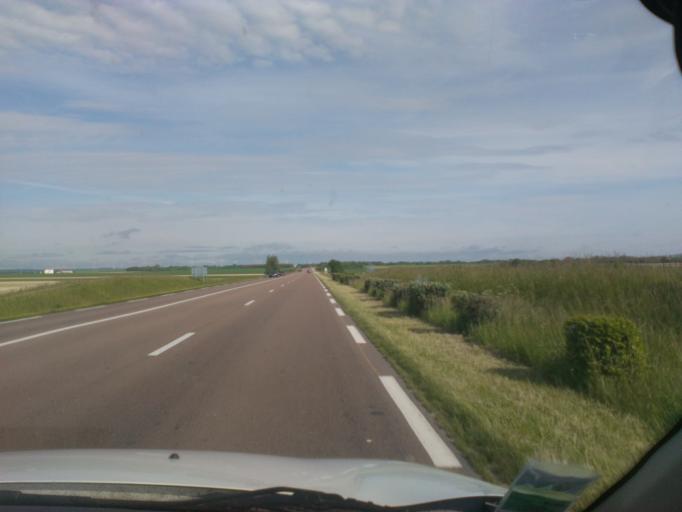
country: FR
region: Champagne-Ardenne
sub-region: Departement de l'Aube
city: La Chapelle-Saint-Luc
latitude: 48.3371
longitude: 4.0163
